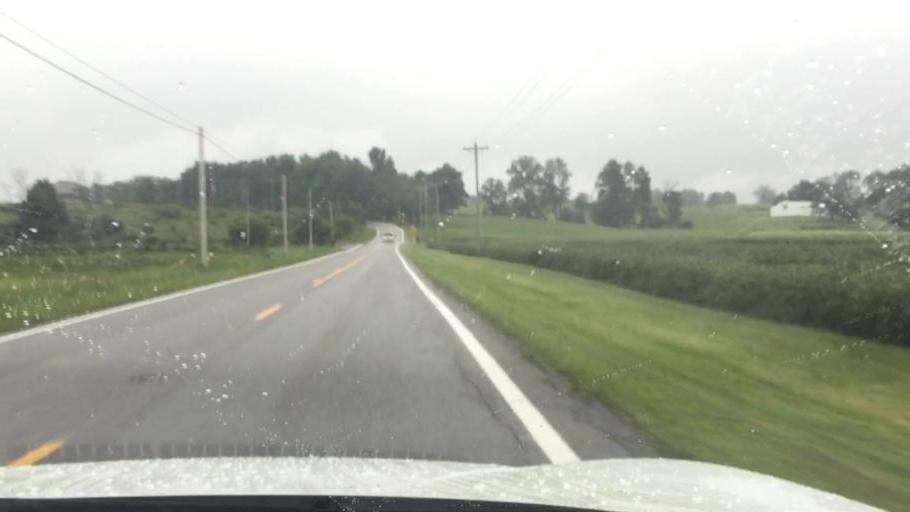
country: US
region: Ohio
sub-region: Champaign County
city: Mechanicsburg
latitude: 40.0229
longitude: -83.6385
